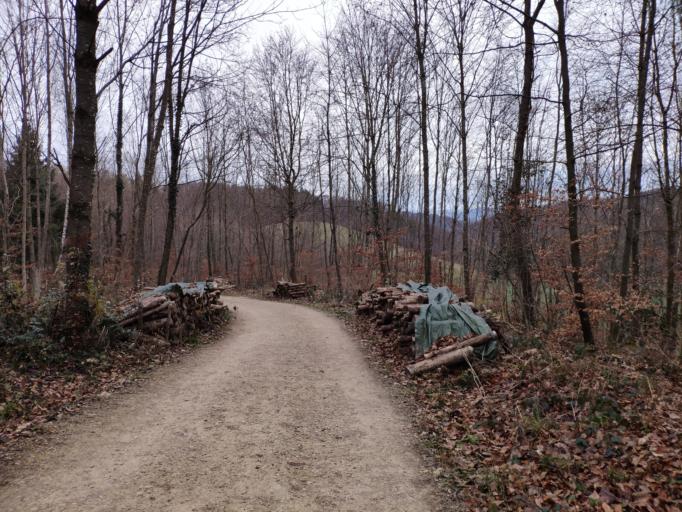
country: CH
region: Basel-City
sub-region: Basel-Stadt
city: Bettingen
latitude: 47.5774
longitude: 7.6775
